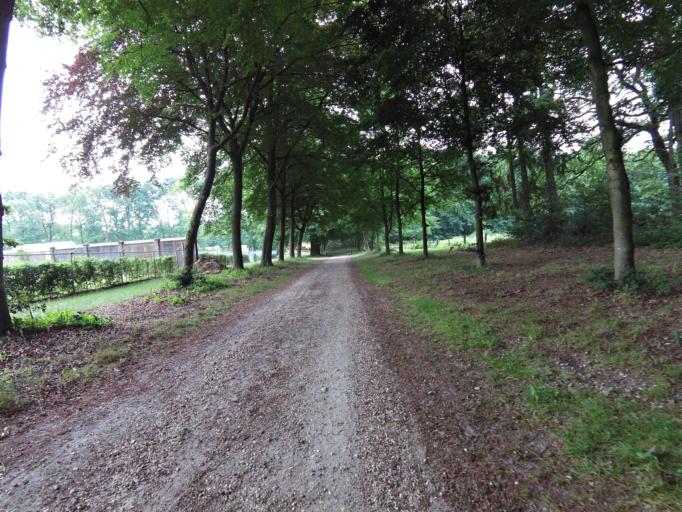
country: NL
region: North Brabant
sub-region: Gemeente Cuijk
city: Cuijk
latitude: 51.7692
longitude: 5.8898
